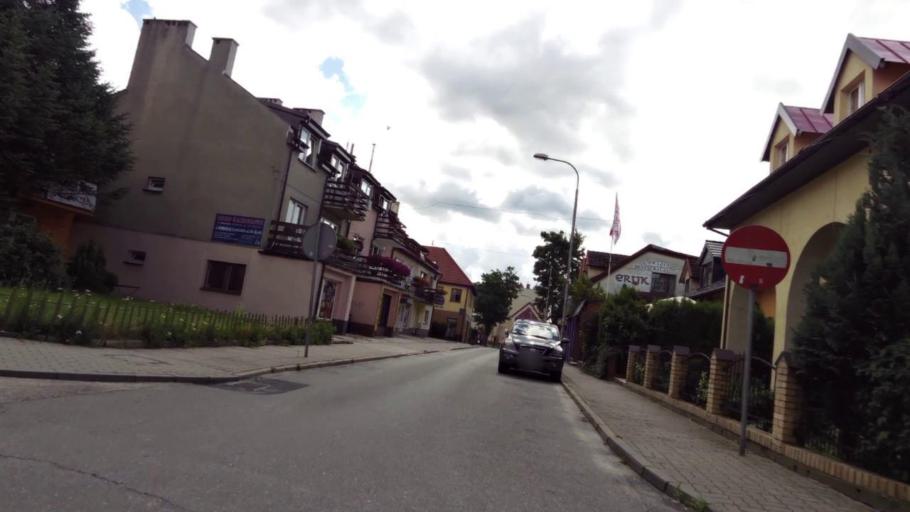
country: PL
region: West Pomeranian Voivodeship
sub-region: Powiat slawienski
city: Darlowo
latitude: 54.4214
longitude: 16.4124
